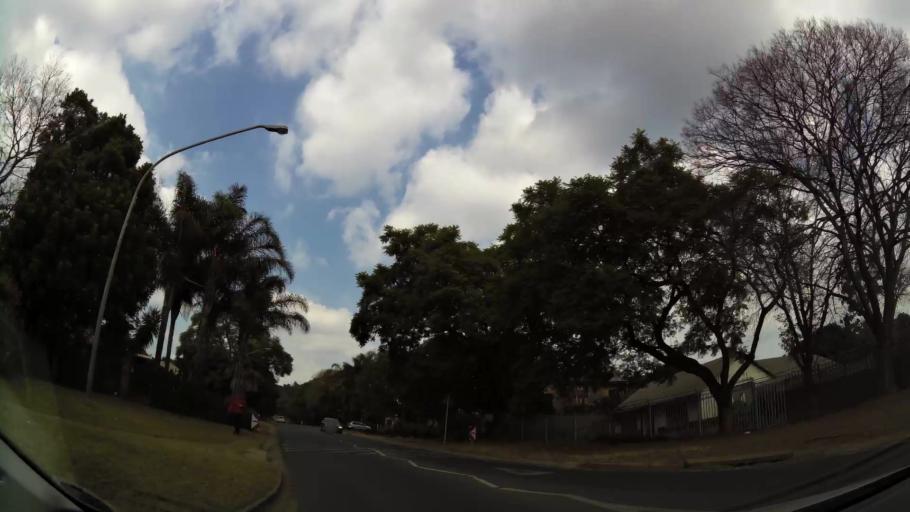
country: ZA
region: Gauteng
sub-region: City of Tshwane Metropolitan Municipality
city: Pretoria
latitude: -25.7626
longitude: 28.3111
